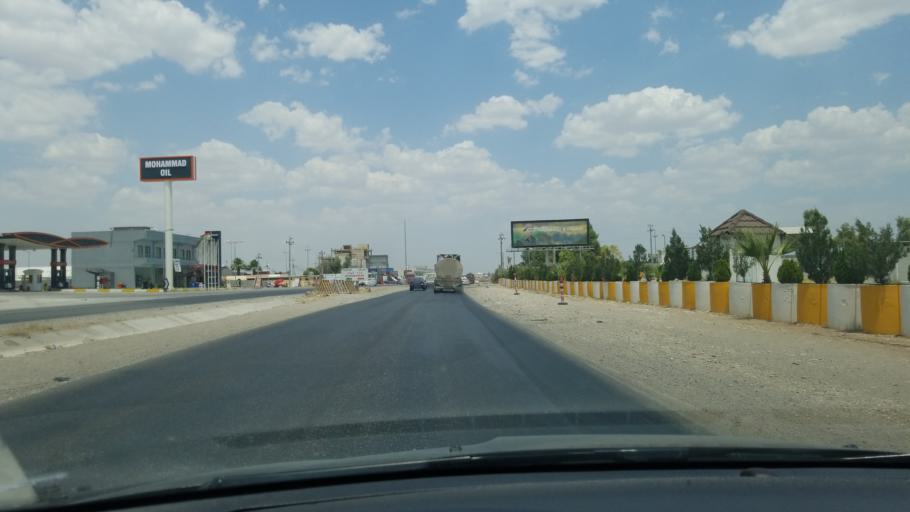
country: IQ
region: Arbil
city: Erbil
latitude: 36.1002
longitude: 44.0211
